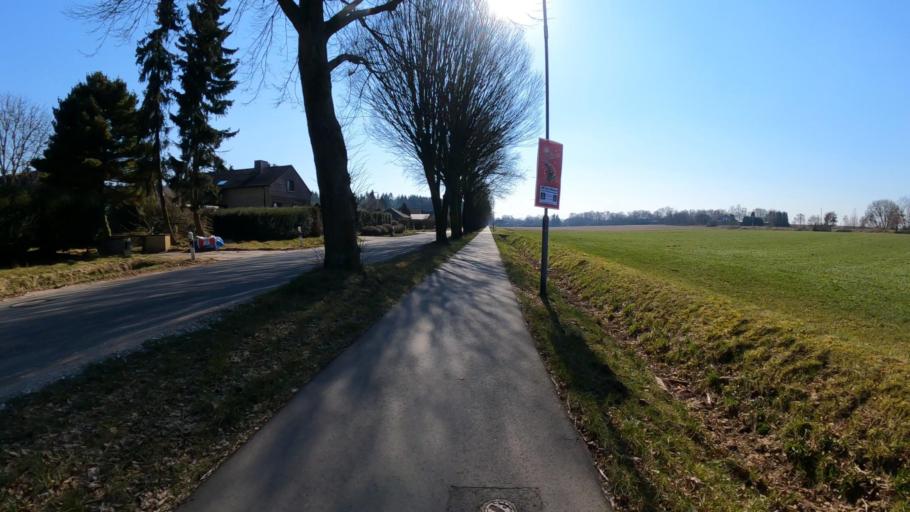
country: DE
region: Lower Saxony
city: Bendestorf
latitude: 53.3590
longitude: 9.9269
